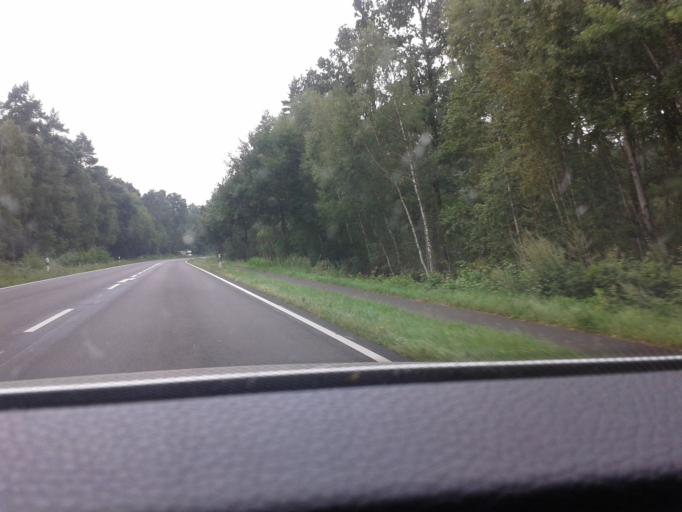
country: DE
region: Lower Saxony
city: Gifhorn
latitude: 52.4971
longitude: 10.5796
